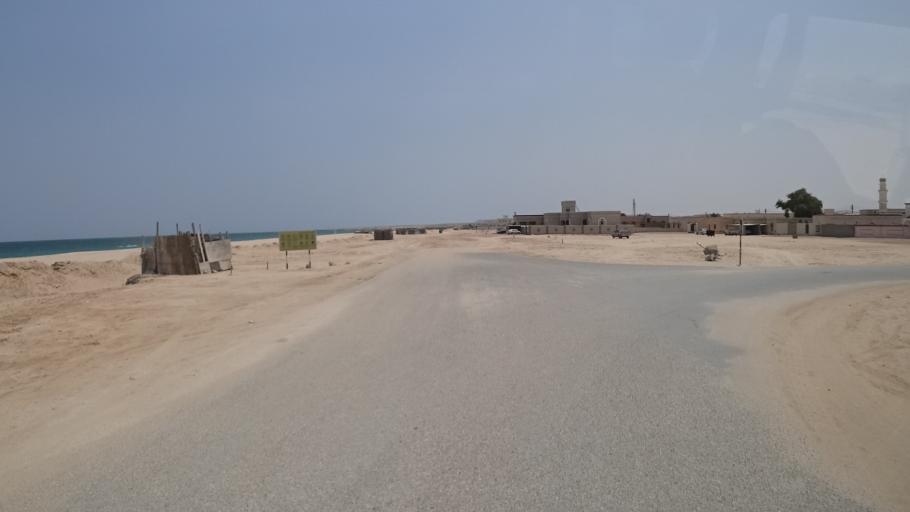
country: OM
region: Ash Sharqiyah
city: Sur
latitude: 22.5217
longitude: 59.7987
